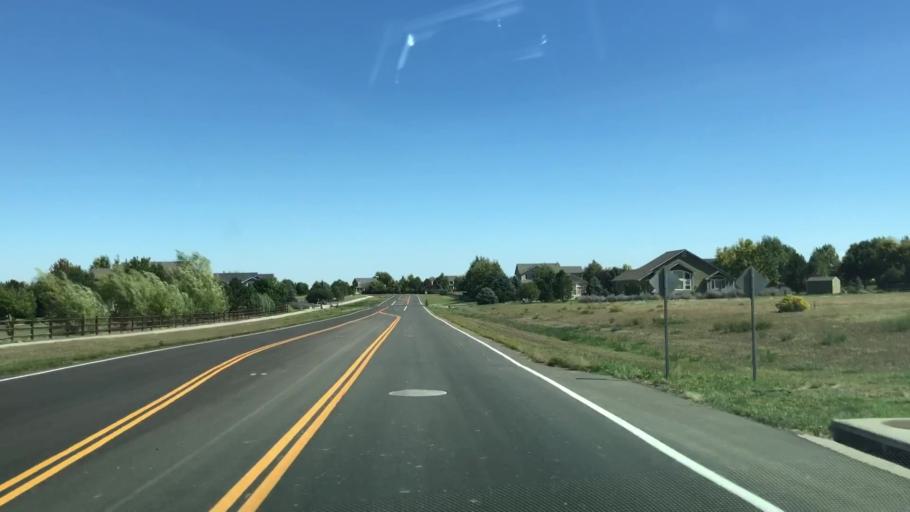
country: US
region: Colorado
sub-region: Weld County
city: Windsor
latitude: 40.4421
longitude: -104.9635
